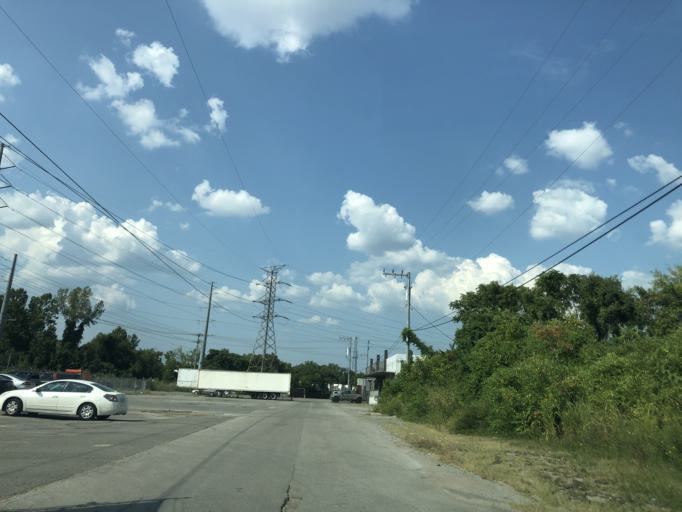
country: US
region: Tennessee
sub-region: Davidson County
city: Oak Hill
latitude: 36.1207
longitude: -86.7705
